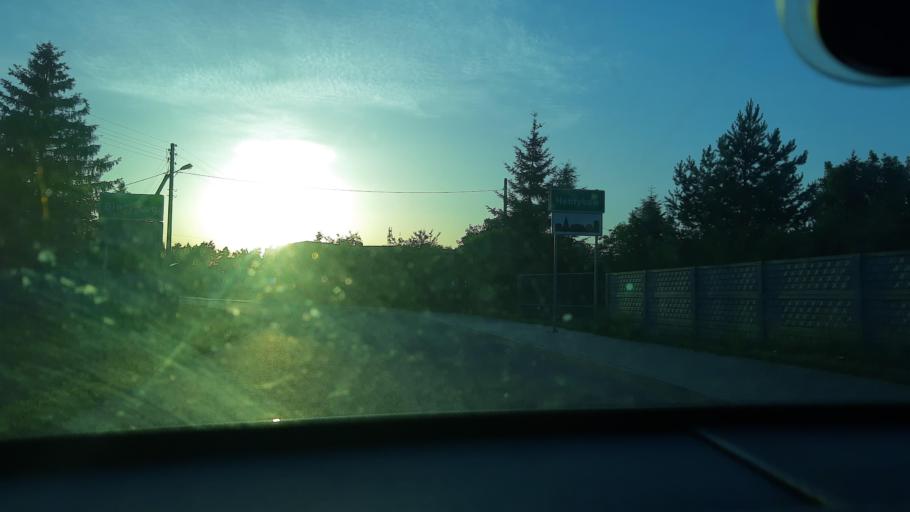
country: PL
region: Lodz Voivodeship
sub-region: Powiat zdunskowolski
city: Zdunska Wola
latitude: 51.6072
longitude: 18.9839
